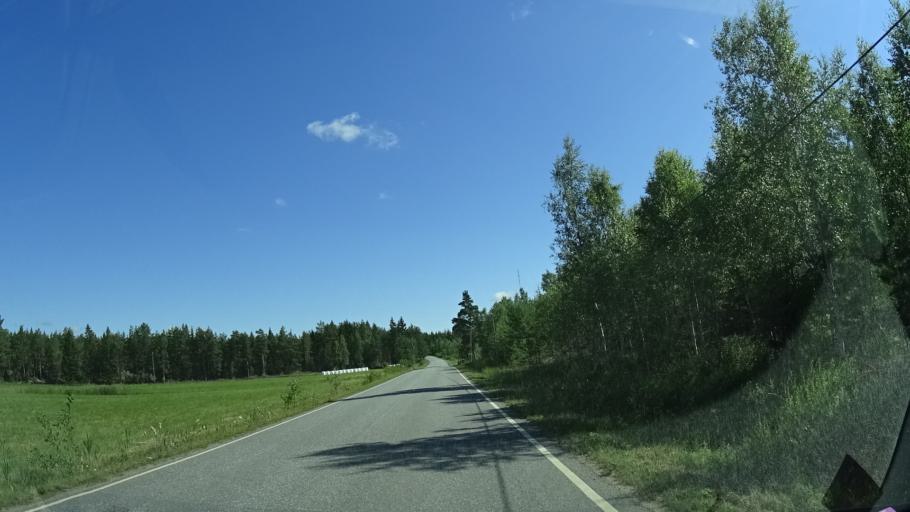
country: FI
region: Varsinais-Suomi
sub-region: Turku
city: Velkua
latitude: 60.4727
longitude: 21.7125
